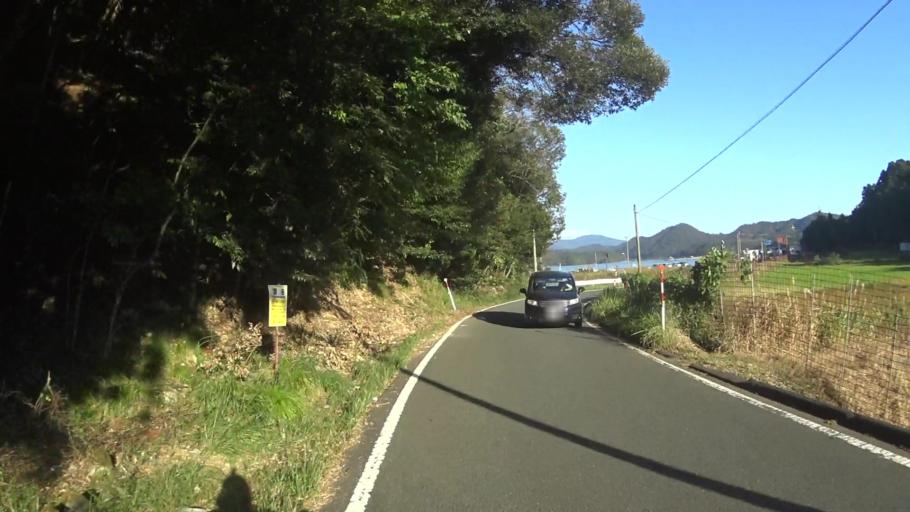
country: JP
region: Hyogo
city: Toyooka
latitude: 35.6118
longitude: 134.8858
